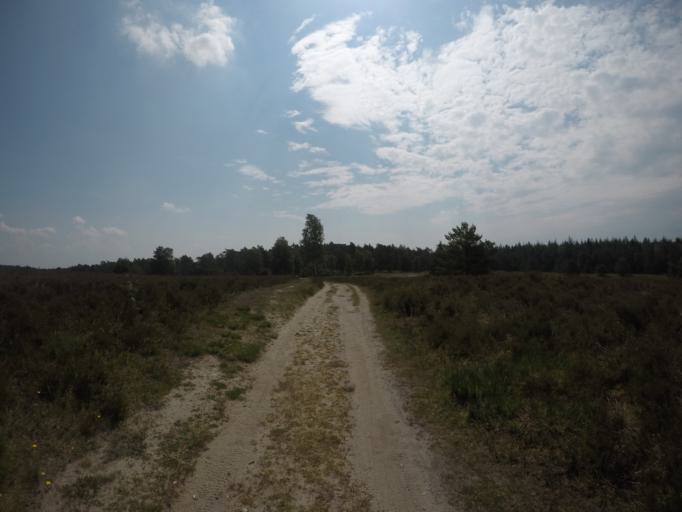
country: DE
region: Lower Saxony
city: Buchholz in der Nordheide
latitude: 53.2973
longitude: 9.8338
